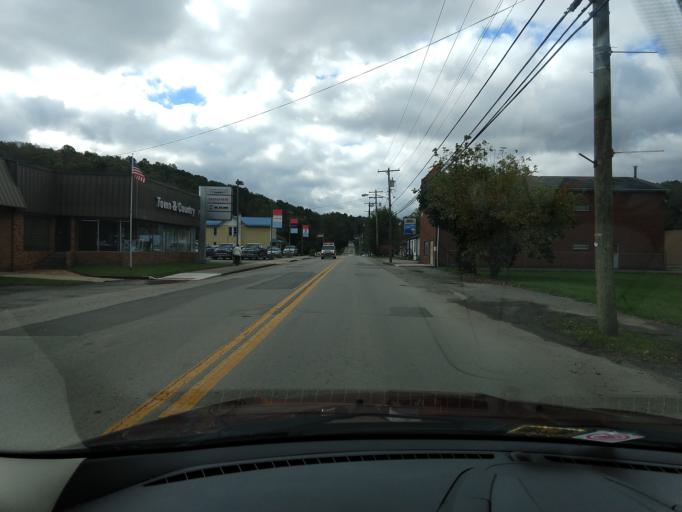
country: US
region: West Virginia
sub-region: Barbour County
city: Belington
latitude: 39.0234
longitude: -79.9365
